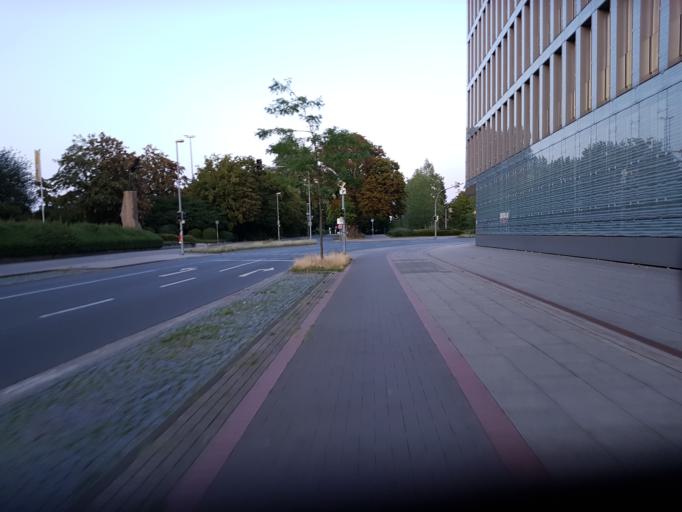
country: DE
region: Lower Saxony
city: Hannover
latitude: 52.4020
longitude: 9.7658
